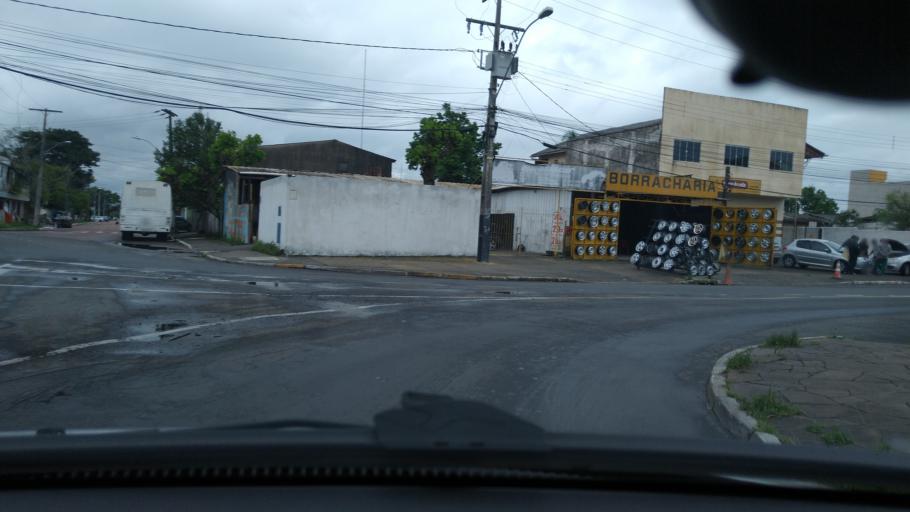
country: BR
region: Rio Grande do Sul
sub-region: Canoas
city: Canoas
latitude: -29.9014
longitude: -51.2166
